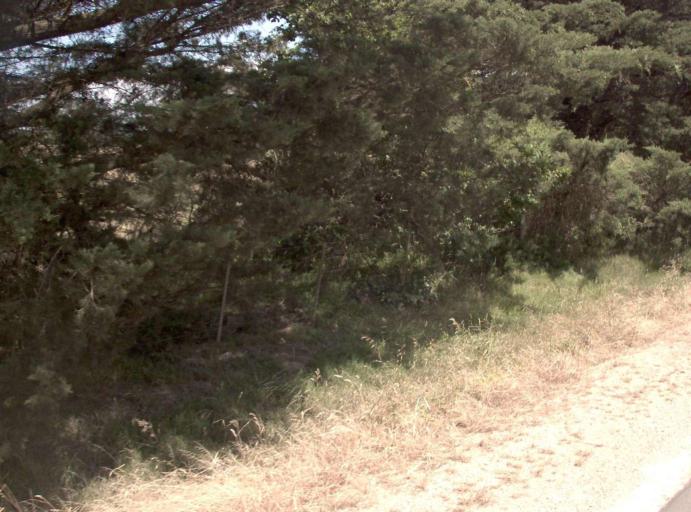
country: AU
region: Victoria
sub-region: Wellington
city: Heyfield
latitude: -38.0285
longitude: 146.8797
